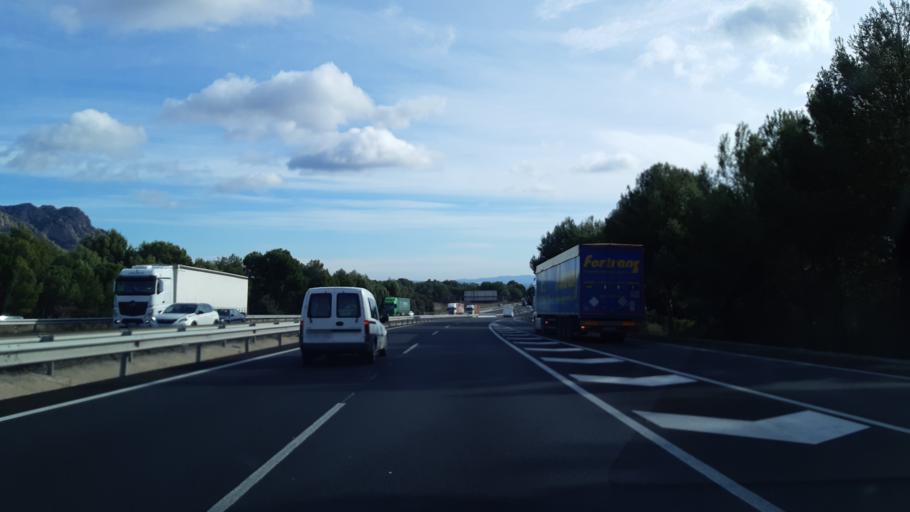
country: ES
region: Catalonia
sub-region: Provincia de Barcelona
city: Collbato
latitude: 41.5722
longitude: 1.7906
